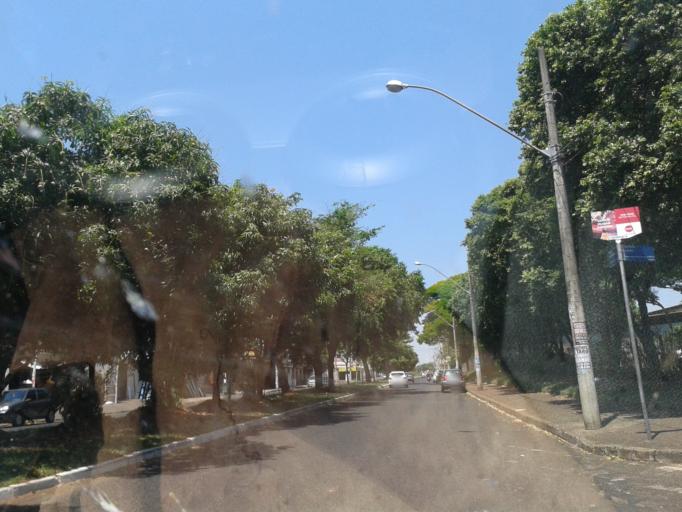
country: BR
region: Minas Gerais
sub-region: Uberlandia
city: Uberlandia
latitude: -18.9349
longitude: -48.3046
